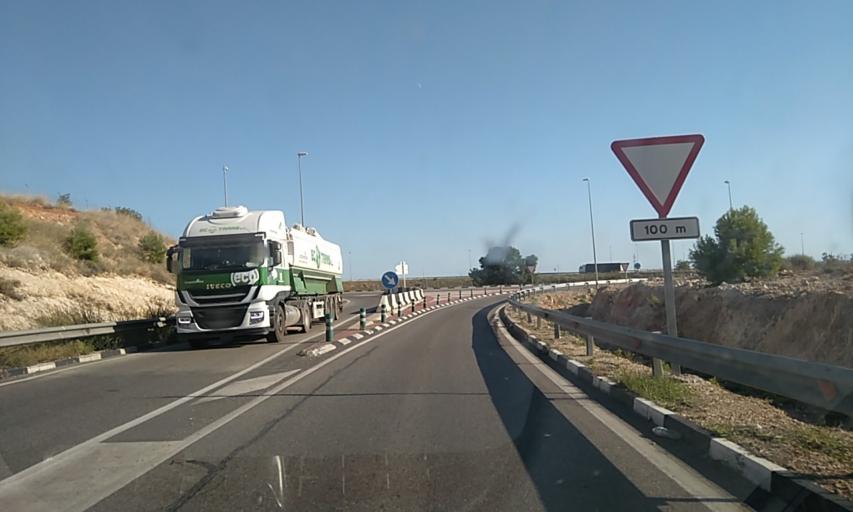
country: ES
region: Valencia
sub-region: Provincia de Castello
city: Torreblanca
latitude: 40.2293
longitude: 0.2124
